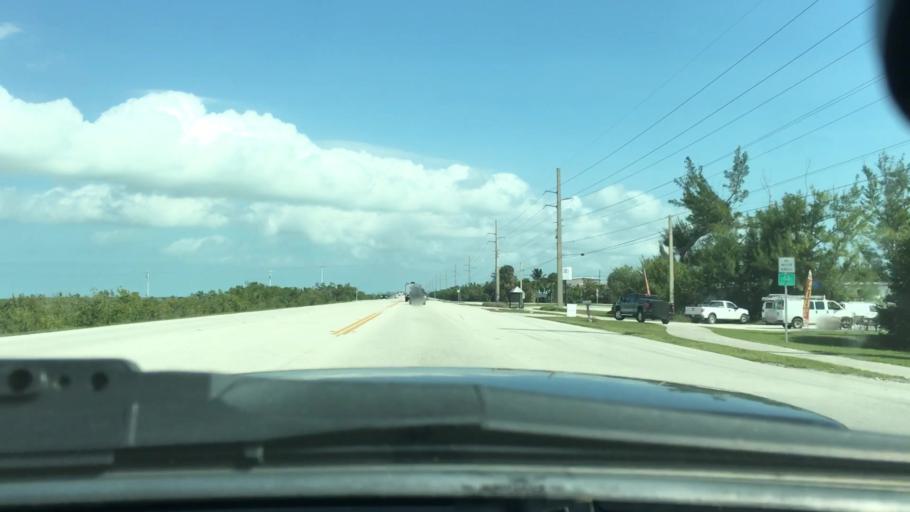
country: US
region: Florida
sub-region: Monroe County
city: Big Coppitt Key
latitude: 24.6283
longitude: -81.5943
